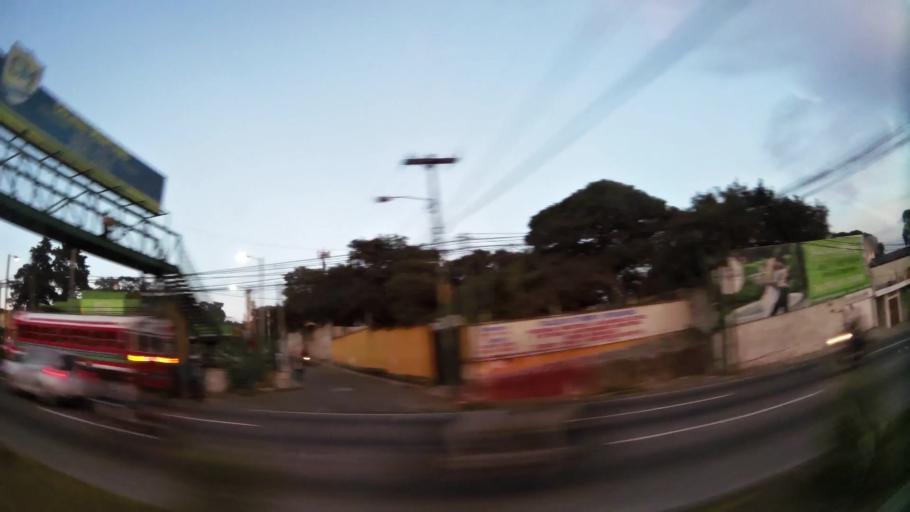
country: GT
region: Guatemala
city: Mixco
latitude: 14.6172
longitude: -90.6103
